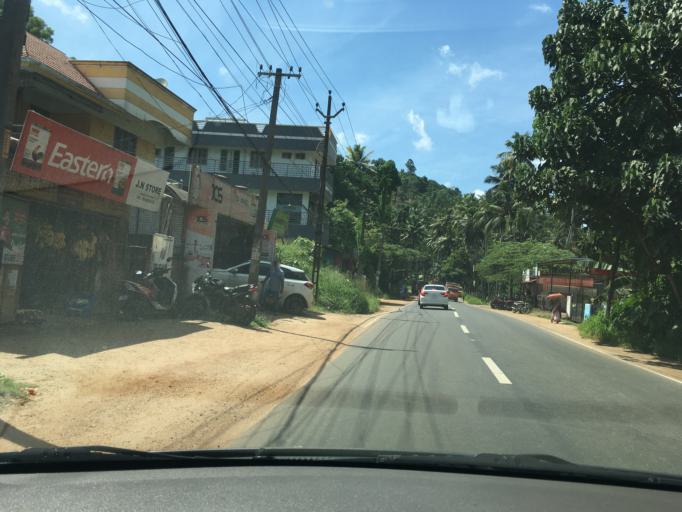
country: IN
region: Kerala
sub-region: Thiruvananthapuram
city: Nedumangad
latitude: 8.5704
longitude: 76.9883
